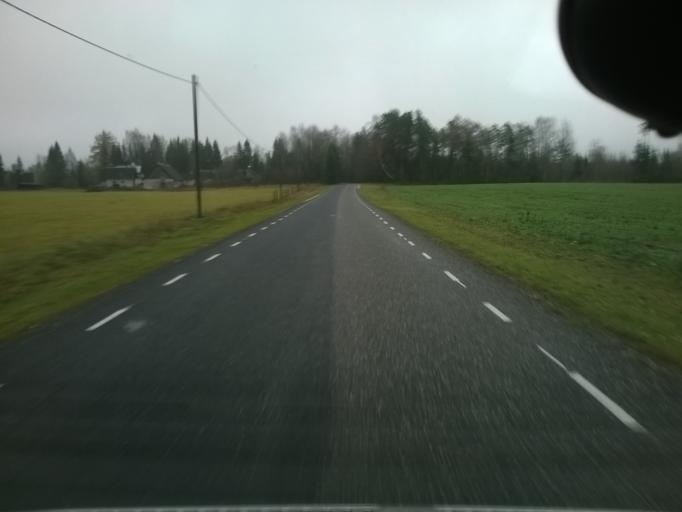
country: EE
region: Harju
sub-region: Saue linn
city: Saue
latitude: 59.1435
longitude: 24.5580
